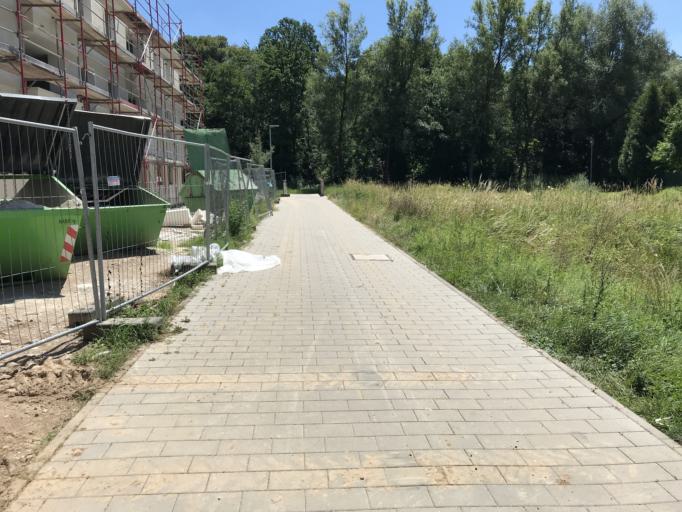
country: DE
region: Baden-Wuerttemberg
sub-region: Freiburg Region
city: Schopfheim
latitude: 47.6450
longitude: 7.8222
